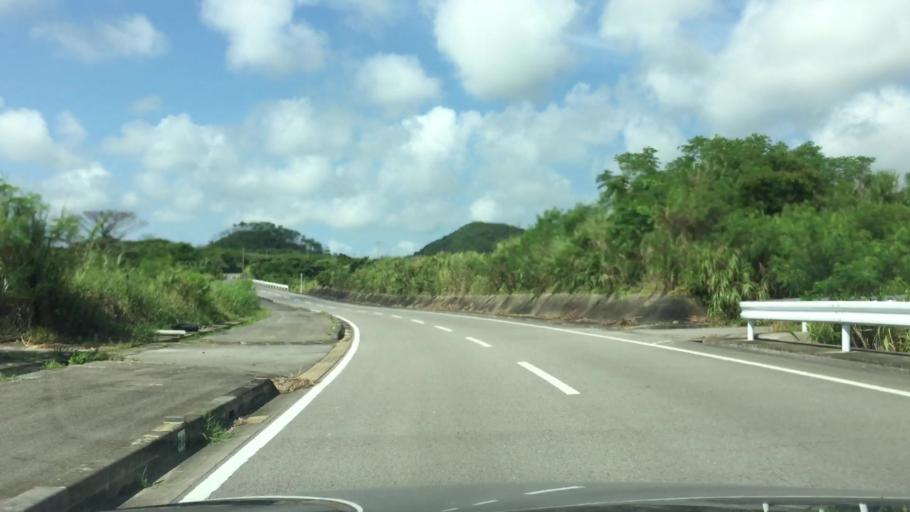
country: JP
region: Okinawa
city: Ishigaki
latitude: 24.4145
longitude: 124.2312
